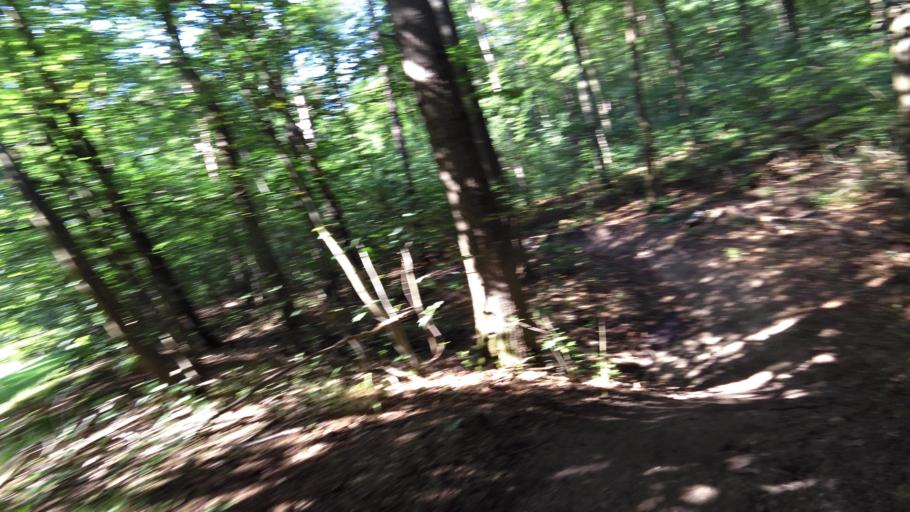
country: NL
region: Gelderland
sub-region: Gemeente Arnhem
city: Gulden Bodem
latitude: 52.0143
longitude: 5.8954
